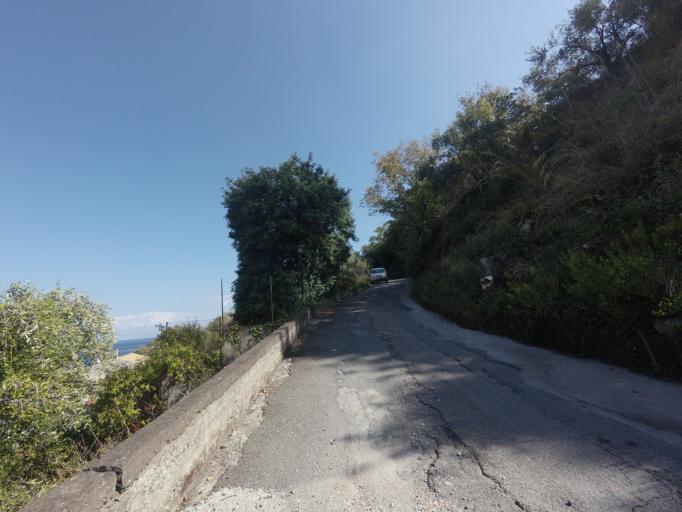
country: IT
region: Sicily
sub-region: Messina
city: Taormina
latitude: 37.8547
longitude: 15.2994
